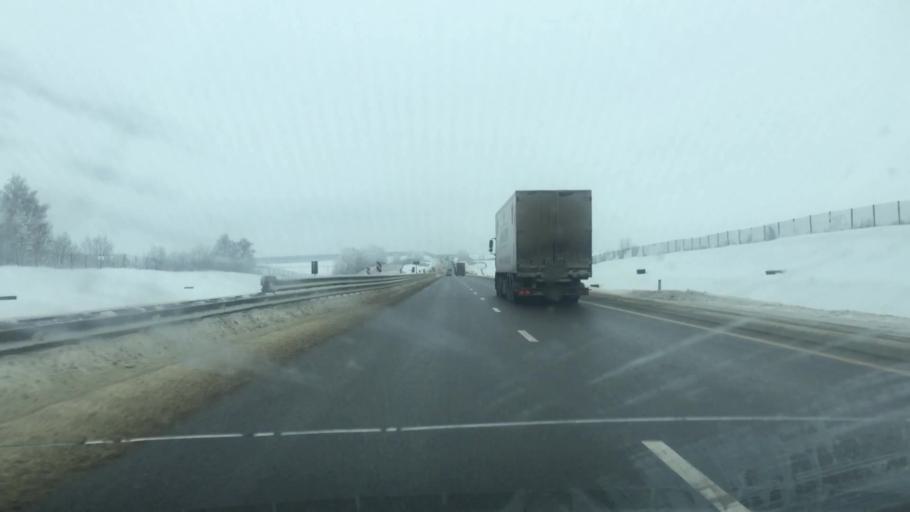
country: RU
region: Tula
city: Kazachka
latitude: 53.3342
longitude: 38.1806
